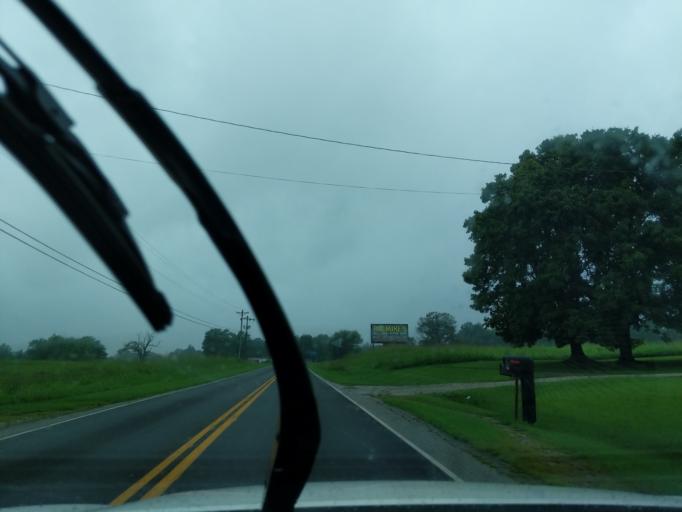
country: US
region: Kentucky
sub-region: Barren County
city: Cave City
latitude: 37.1326
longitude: -86.0328
